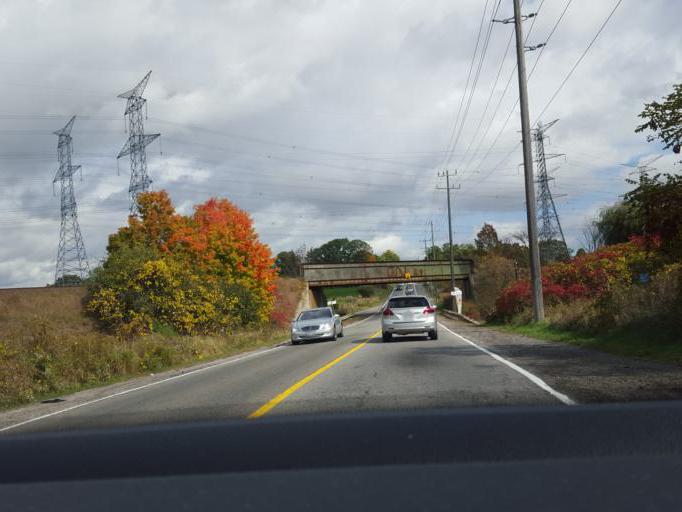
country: CA
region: Ontario
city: Markham
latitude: 43.8452
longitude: -79.2132
